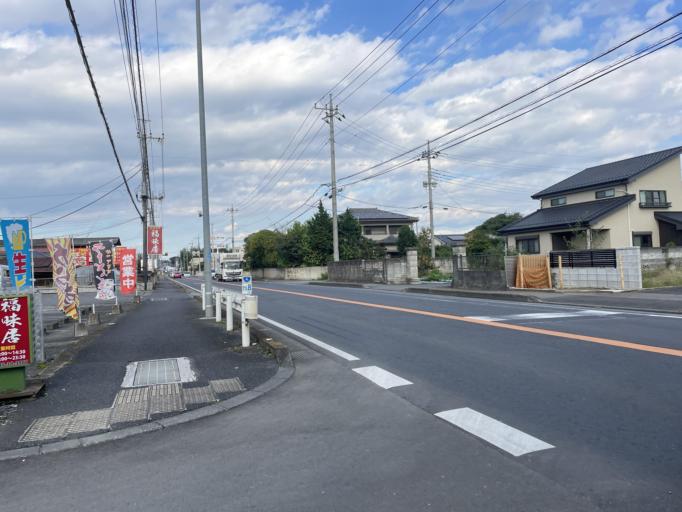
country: JP
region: Tochigi
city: Oyama
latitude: 36.2812
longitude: 139.7766
